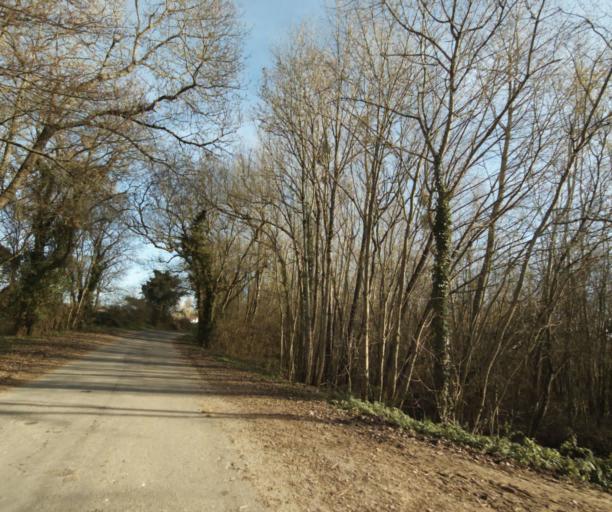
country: FR
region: Poitou-Charentes
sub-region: Departement de la Charente-Maritime
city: Chaniers
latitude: 45.7091
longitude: -0.5346
